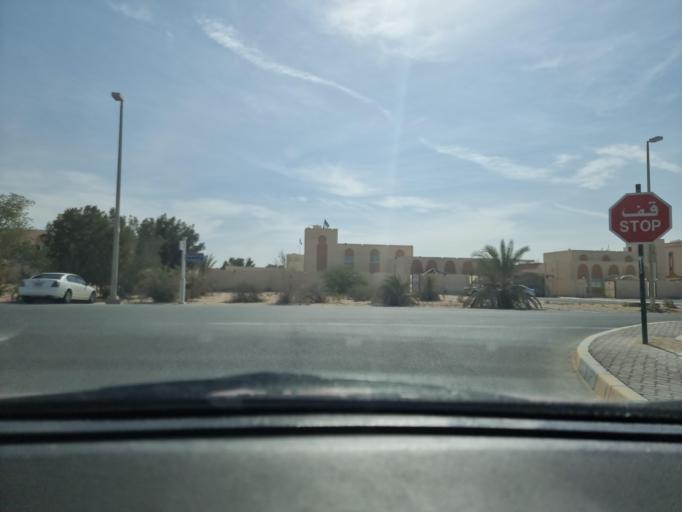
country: AE
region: Abu Dhabi
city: Abu Dhabi
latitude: 24.3844
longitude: 54.6977
